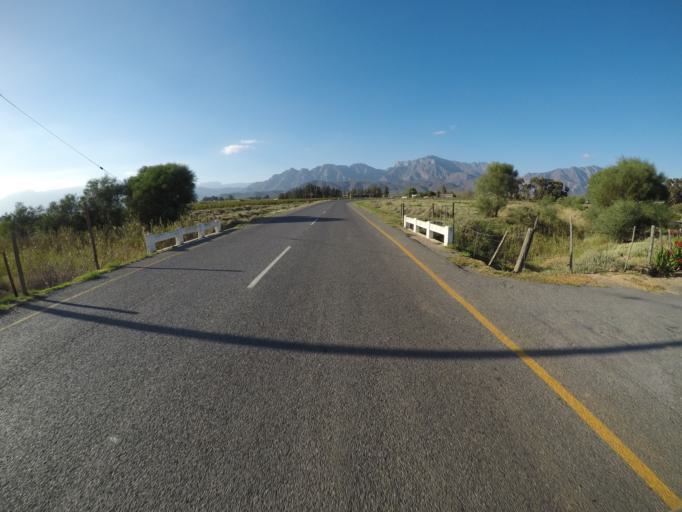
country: ZA
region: Western Cape
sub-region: Cape Winelands District Municipality
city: Worcester
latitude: -33.6675
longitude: 19.5428
